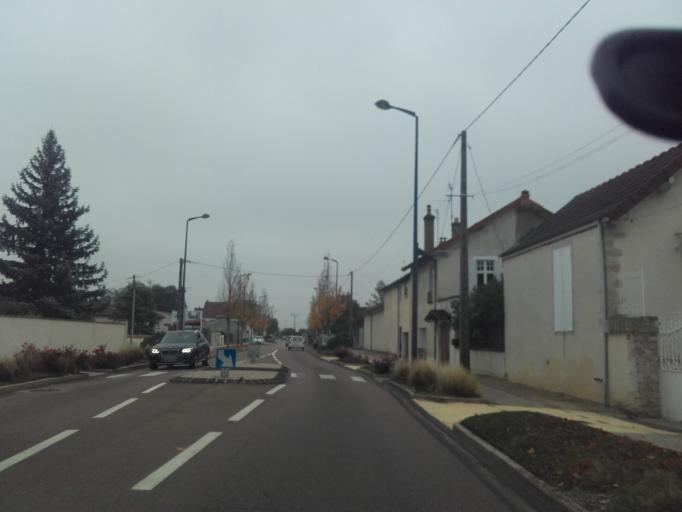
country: FR
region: Bourgogne
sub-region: Departement de la Cote-d'Or
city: Beaune
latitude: 47.0197
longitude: 4.8533
